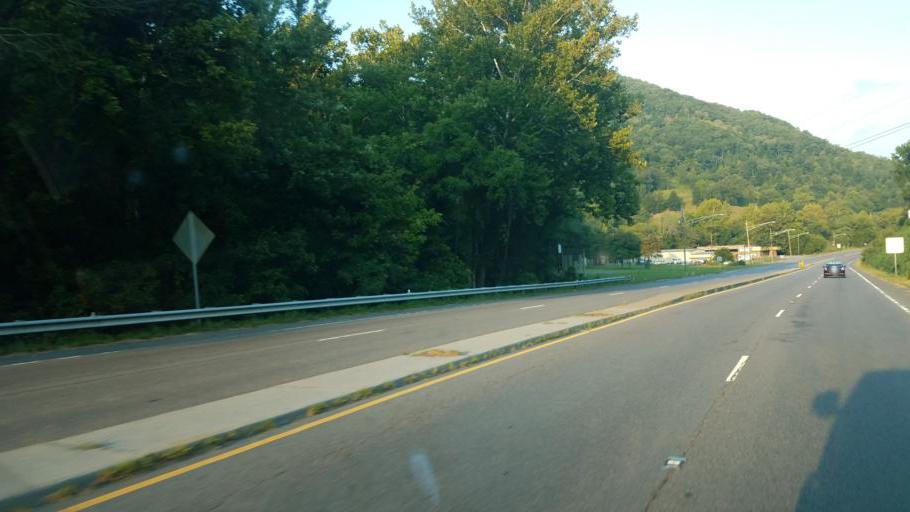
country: US
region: Virginia
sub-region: Scott County
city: Weber City
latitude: 36.6379
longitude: -82.5635
